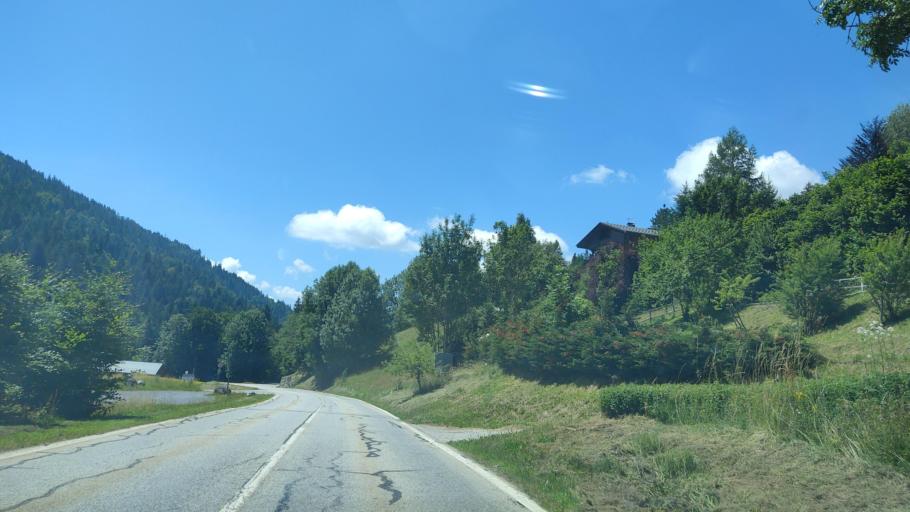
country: FR
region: Rhone-Alpes
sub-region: Departement de la Haute-Savoie
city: Praz-sur-Arly
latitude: 45.8086
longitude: 6.5043
